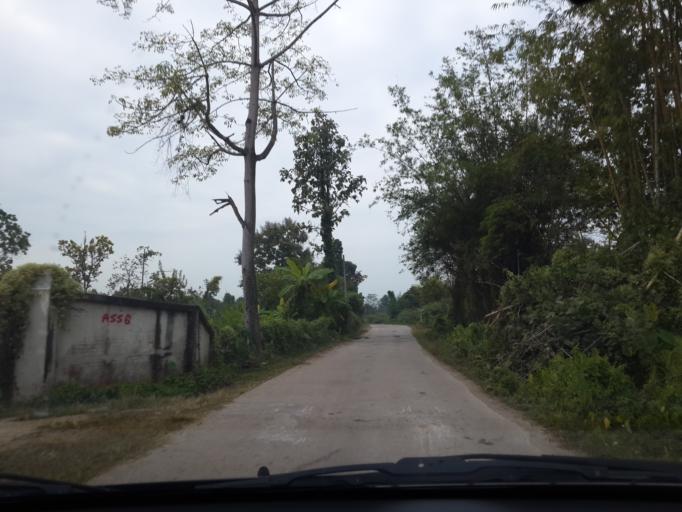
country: TH
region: Chiang Mai
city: San Sai
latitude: 18.9111
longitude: 99.1088
